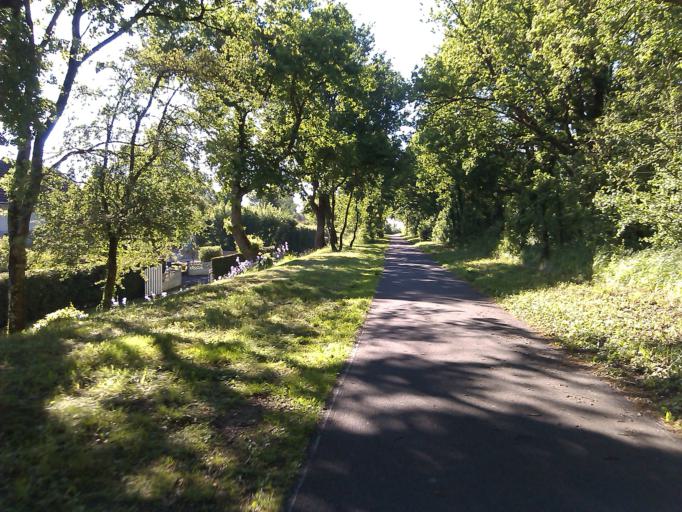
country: FR
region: Centre
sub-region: Departement de l'Indre
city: Le Blanc
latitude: 46.6374
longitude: 1.0761
